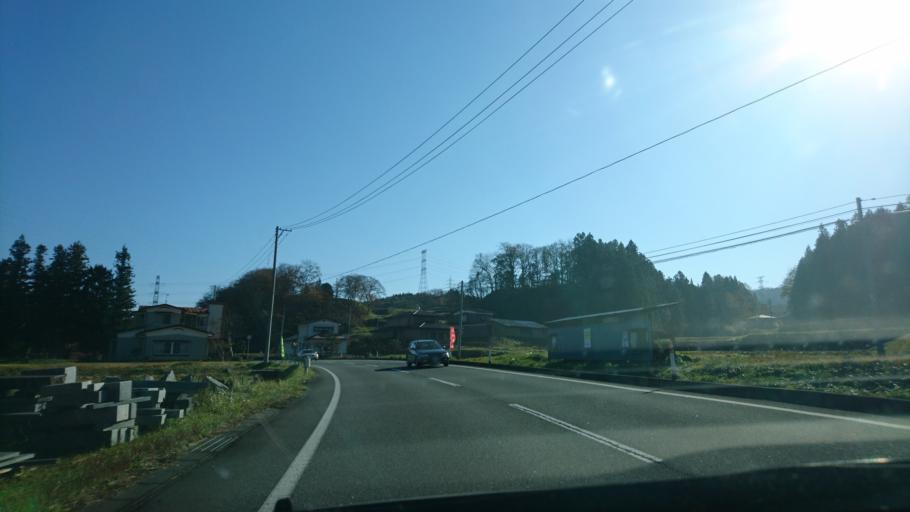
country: JP
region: Iwate
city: Ichinoseki
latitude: 38.9924
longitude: 141.2929
